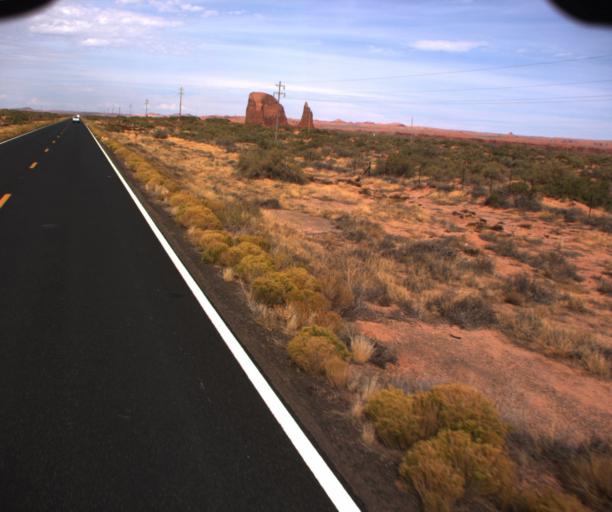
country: US
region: Arizona
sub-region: Apache County
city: Many Farms
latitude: 36.6380
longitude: -109.5876
